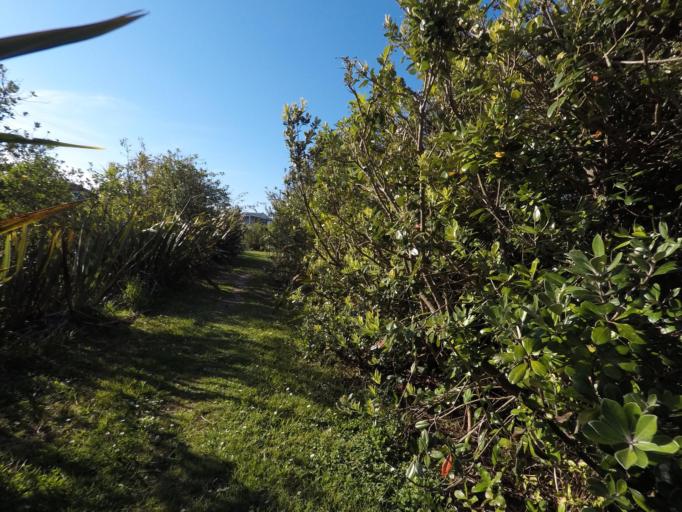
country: NZ
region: Auckland
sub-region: Auckland
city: Rosebank
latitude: -36.8380
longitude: 174.6616
